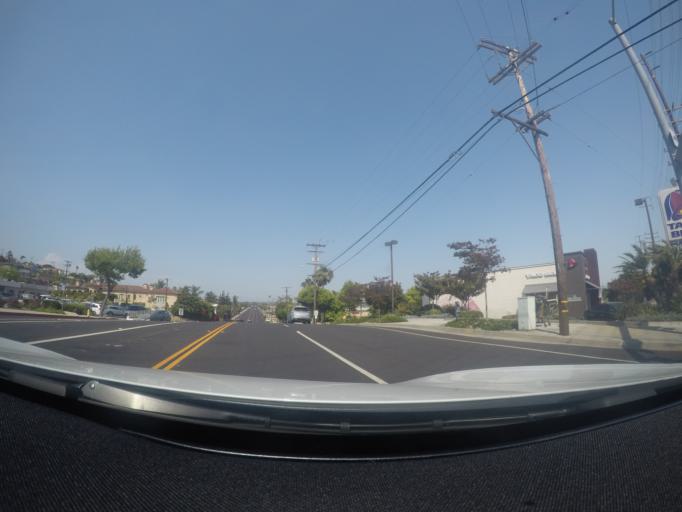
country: US
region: California
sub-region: Los Angeles County
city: Palos Verdes Estates
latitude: 33.8135
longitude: -118.3693
